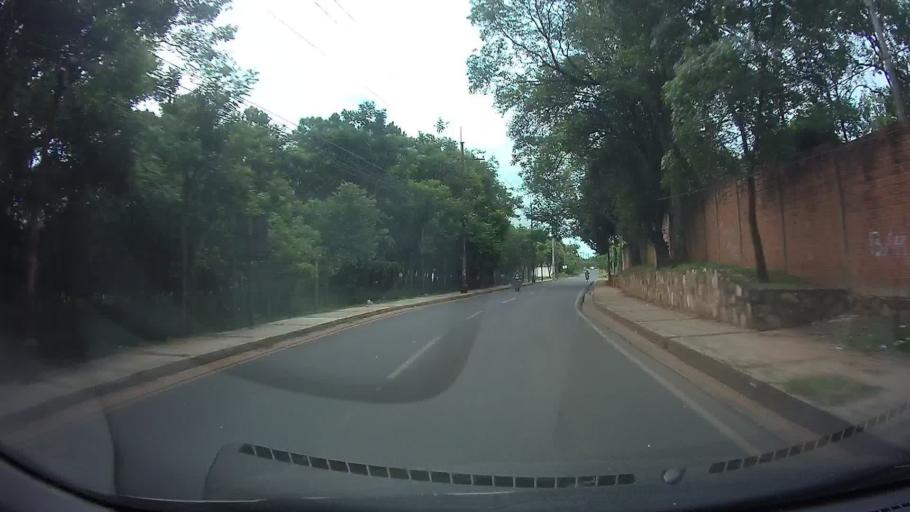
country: PY
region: Central
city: San Lorenzo
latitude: -25.3000
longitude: -57.4914
